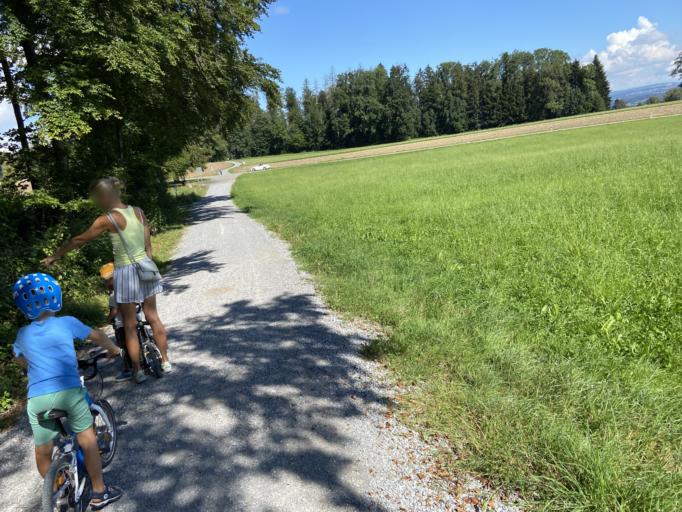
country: CH
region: Zurich
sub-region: Bezirk Meilen
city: Oetwil am See
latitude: 47.2624
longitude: 8.7225
